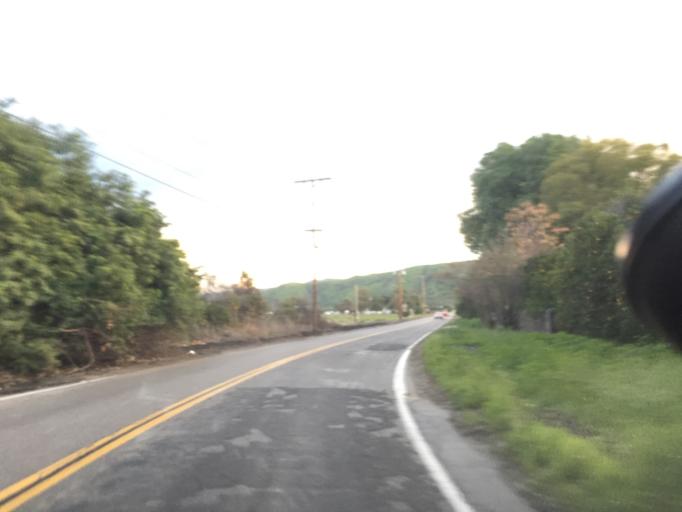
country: US
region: California
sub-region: San Bernardino County
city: Redlands
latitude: 34.0459
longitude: -117.2174
